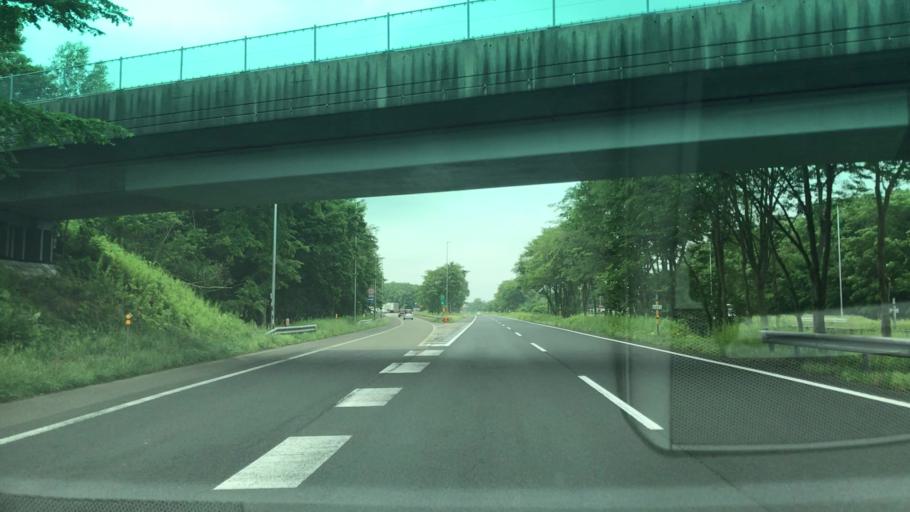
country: JP
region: Hokkaido
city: Chitose
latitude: 42.7541
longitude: 141.6435
